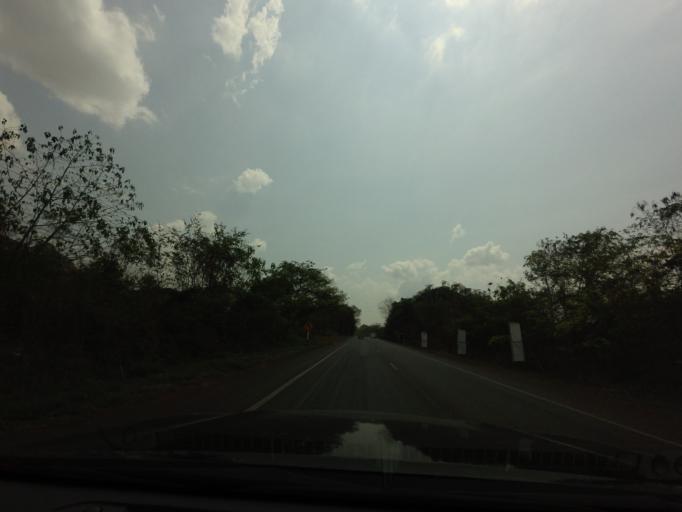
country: TH
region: Kanchanaburi
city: Sai Yok
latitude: 14.1422
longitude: 99.1473
